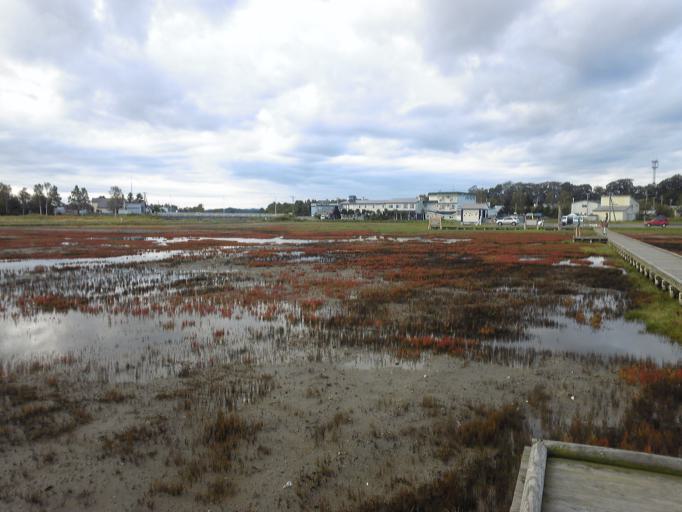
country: JP
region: Hokkaido
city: Abashiri
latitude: 44.0140
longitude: 144.1164
